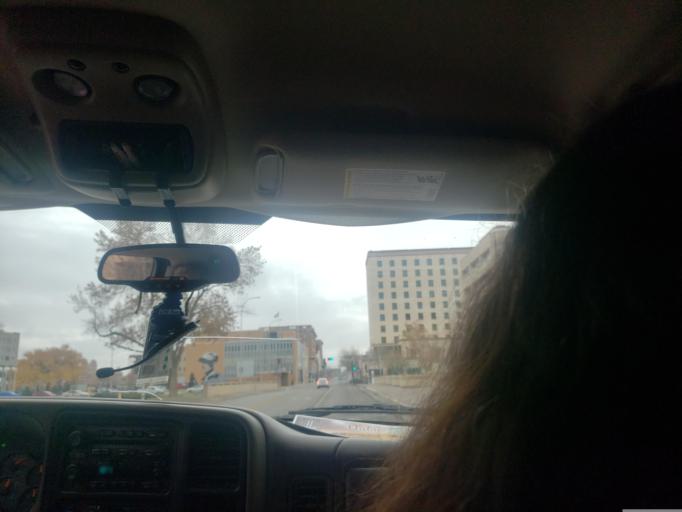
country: US
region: New Mexico
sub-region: Bernalillo County
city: Albuquerque
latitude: 35.0866
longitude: -106.6489
